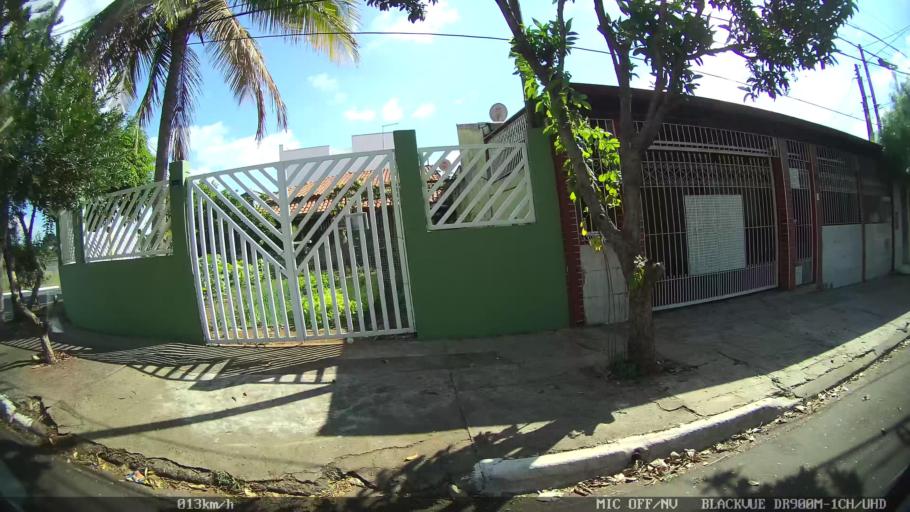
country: BR
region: Sao Paulo
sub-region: Hortolandia
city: Hortolandia
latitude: -22.8939
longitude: -47.2004
